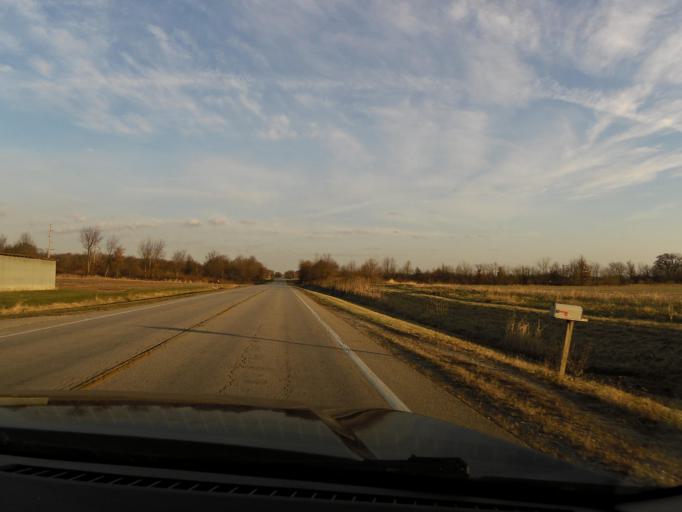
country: US
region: Illinois
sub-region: Fayette County
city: Vandalia
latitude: 38.8875
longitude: -89.0858
